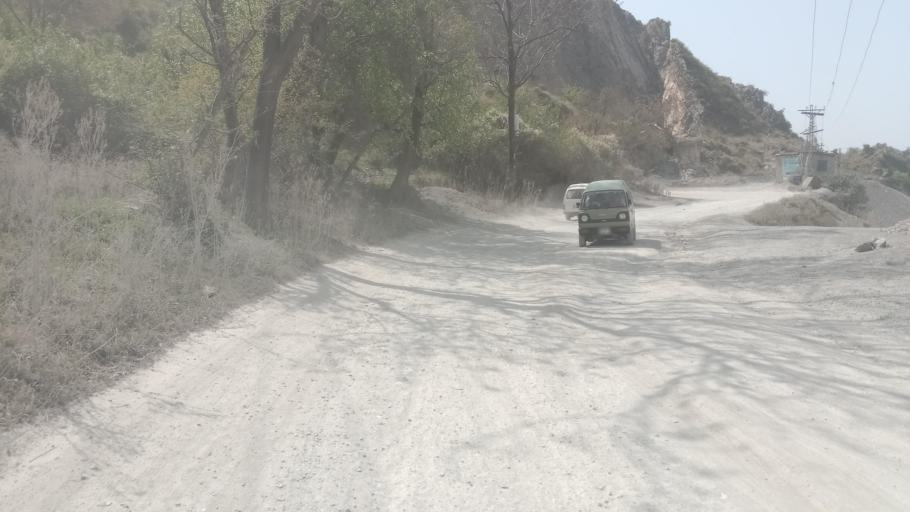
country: PK
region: Khyber Pakhtunkhwa
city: Abbottabad
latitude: 34.1617
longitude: 73.2753
